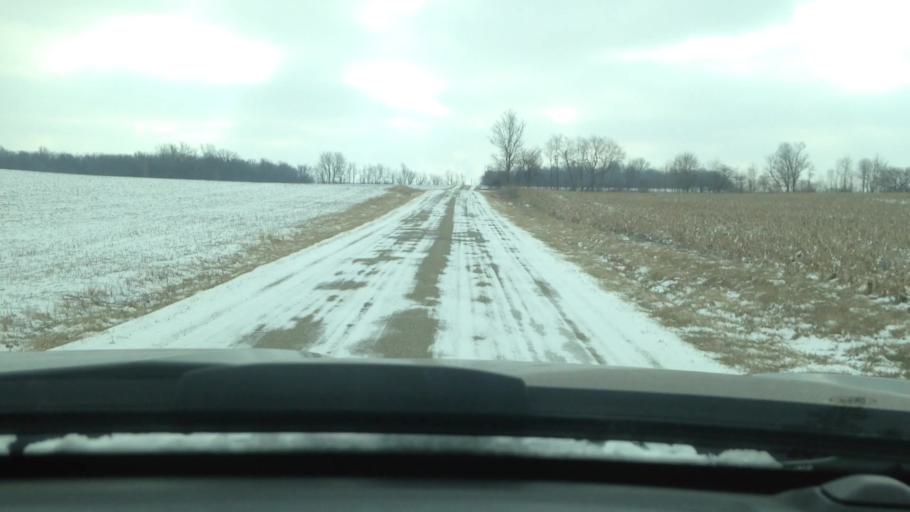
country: US
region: Indiana
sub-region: Randolph County
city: Union City
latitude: 40.2604
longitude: -84.8621
